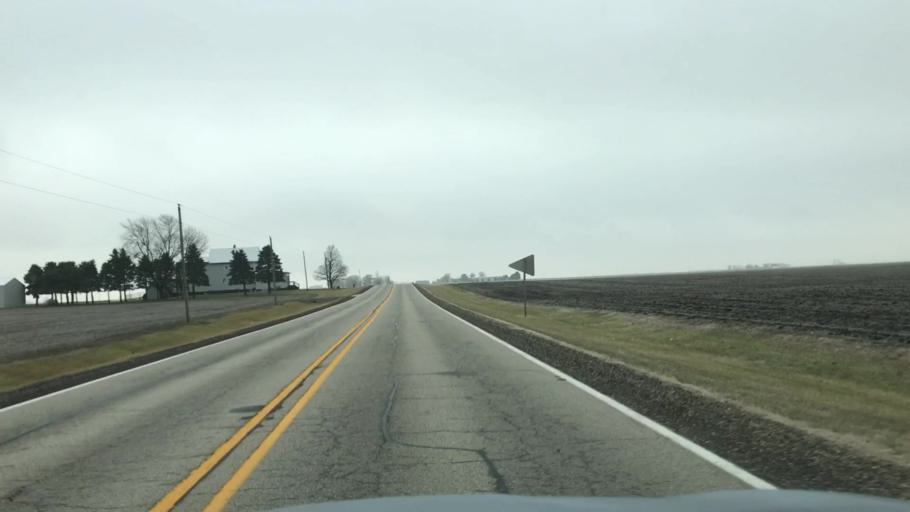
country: US
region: Illinois
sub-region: McLean County
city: Hudson
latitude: 40.6017
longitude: -88.9450
